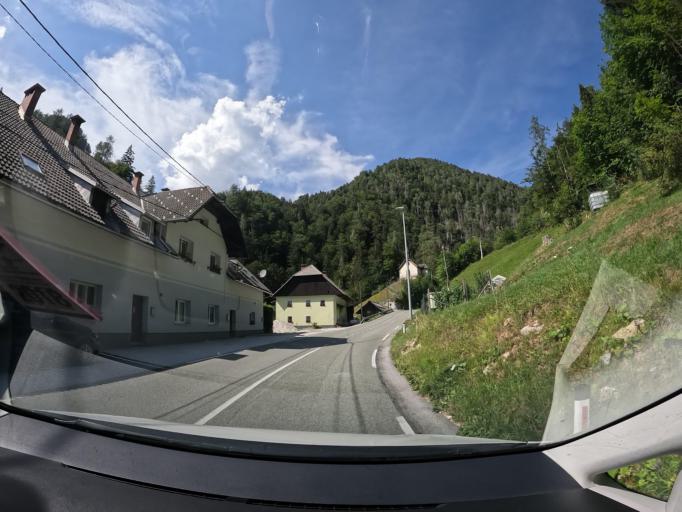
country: SI
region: Trzic
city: Trzic
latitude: 46.4106
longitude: 14.3025
